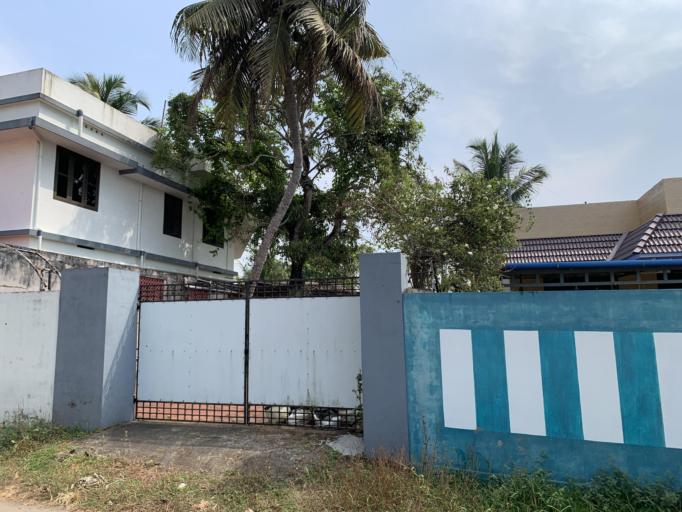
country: IN
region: Kerala
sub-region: Ernakulam
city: Cochin
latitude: 9.9133
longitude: 76.2642
